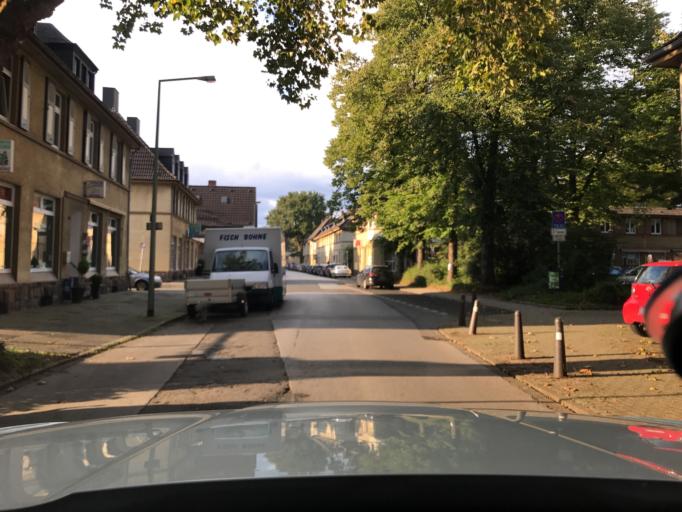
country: DE
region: North Rhine-Westphalia
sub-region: Regierungsbezirk Dusseldorf
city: Hochfeld
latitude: 51.3914
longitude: 6.7966
